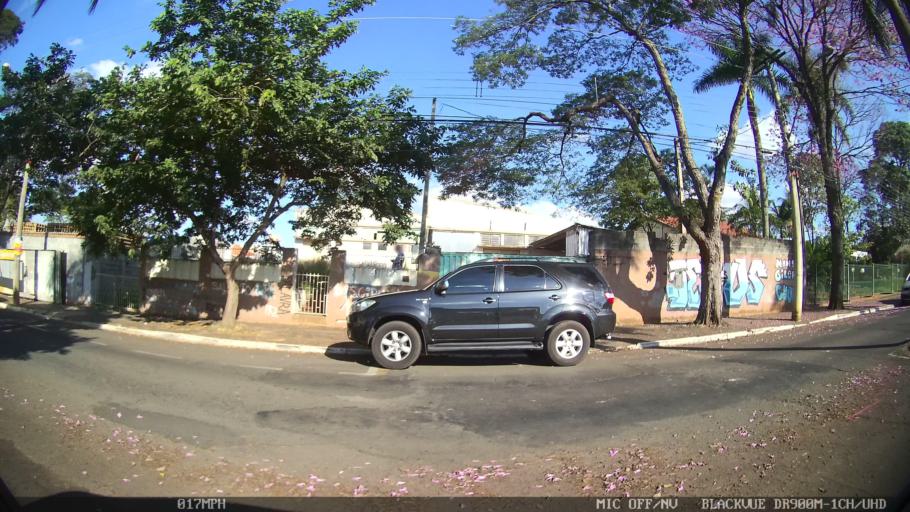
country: BR
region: Sao Paulo
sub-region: Nova Odessa
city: Nova Odessa
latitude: -22.7790
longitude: -47.2972
